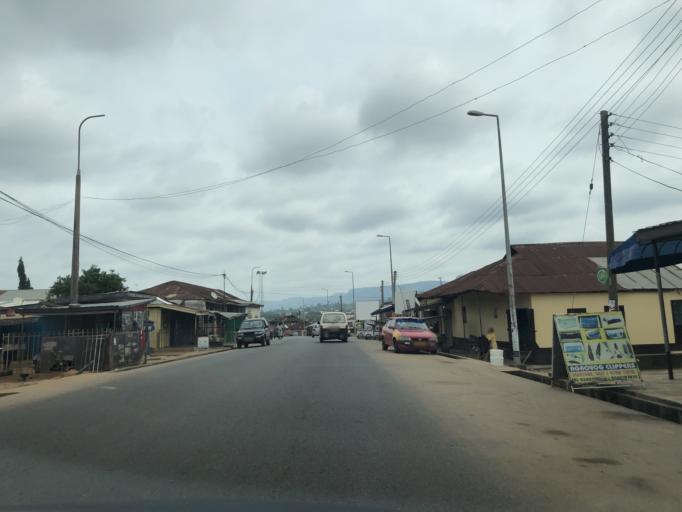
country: GH
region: Eastern
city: Koforidua
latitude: 6.1074
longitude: -0.2676
